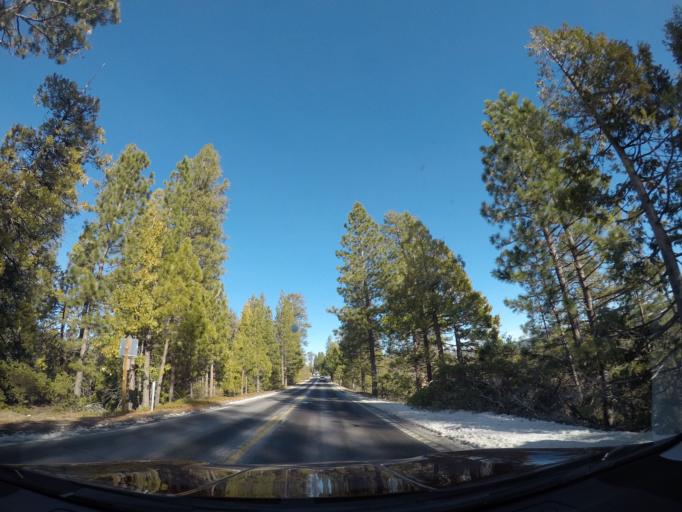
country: US
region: California
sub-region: Tuolumne County
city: Twain Harte
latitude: 38.1509
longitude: -120.0692
